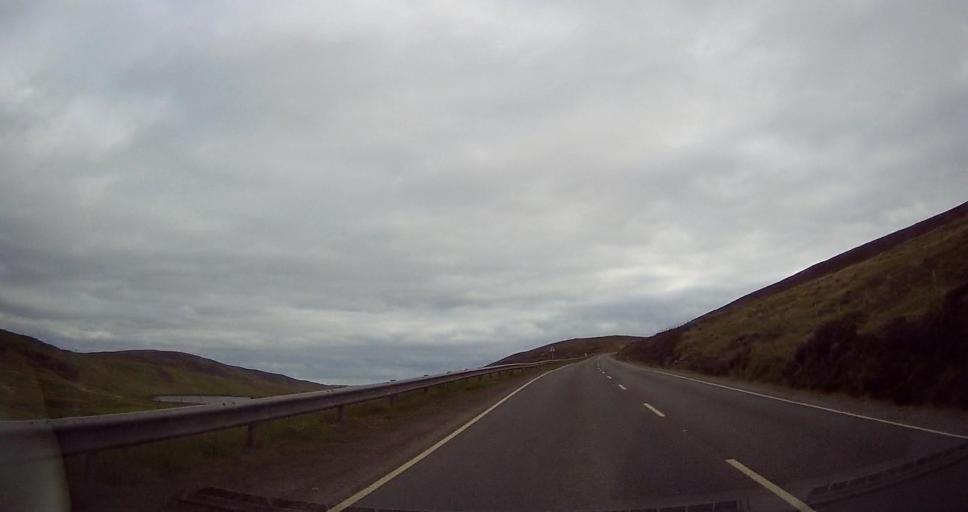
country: GB
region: Scotland
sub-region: Shetland Islands
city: Lerwick
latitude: 60.1618
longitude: -1.2209
